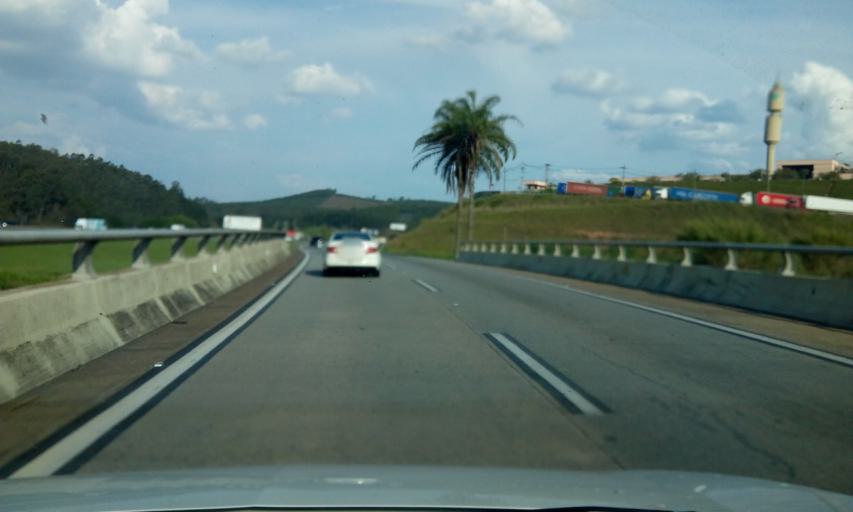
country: BR
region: Sao Paulo
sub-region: Varzea Paulista
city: Varzea Paulista
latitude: -23.2633
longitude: -46.8663
